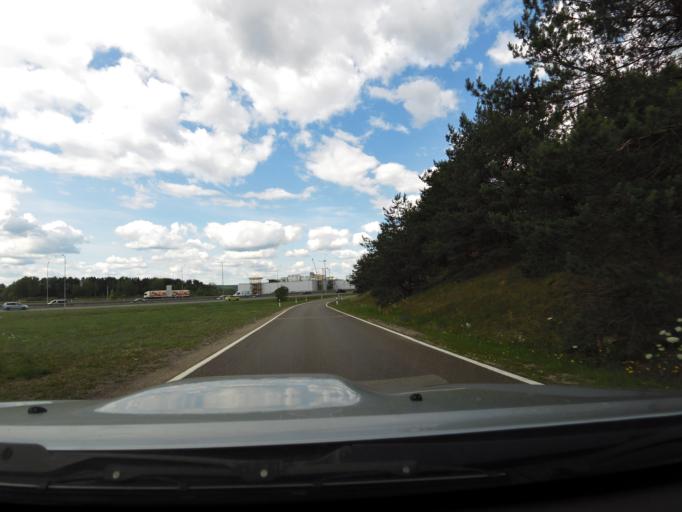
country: LT
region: Vilnius County
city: Pilaite
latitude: 54.6554
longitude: 25.1535
